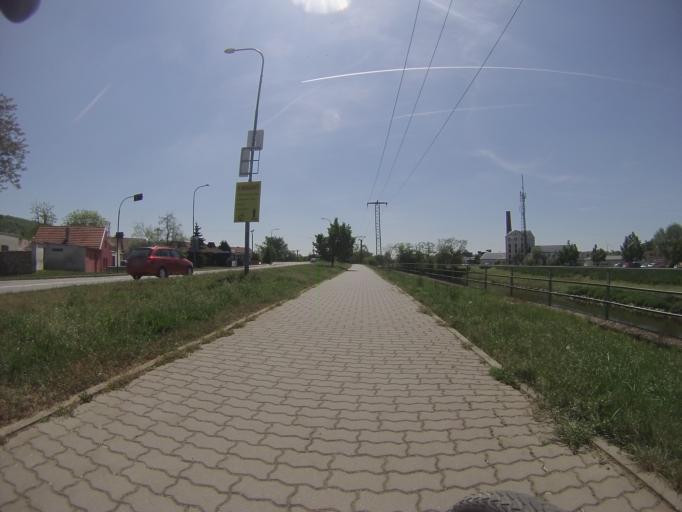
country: CZ
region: South Moravian
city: Zidlochovice
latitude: 49.0363
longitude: 16.6167
